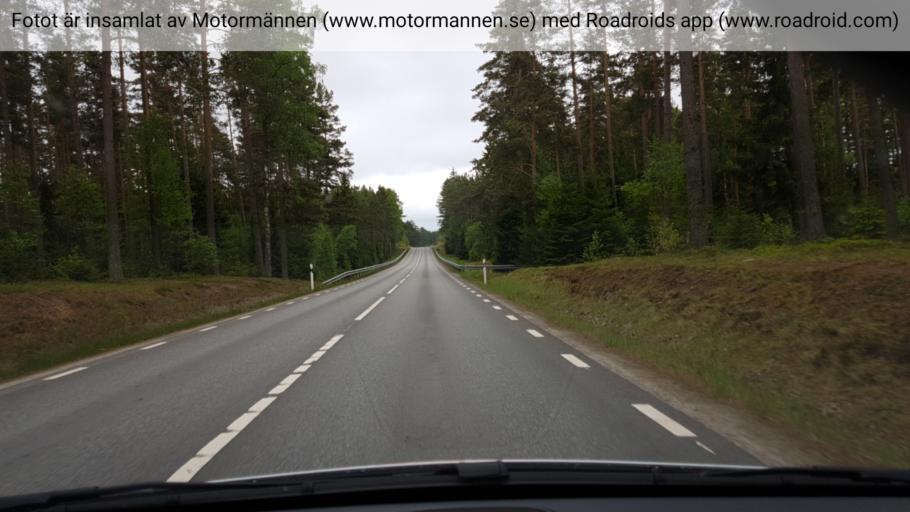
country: SE
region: Joenkoeping
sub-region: Mullsjo Kommun
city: Mullsjoe
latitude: 57.8862
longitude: 13.8475
